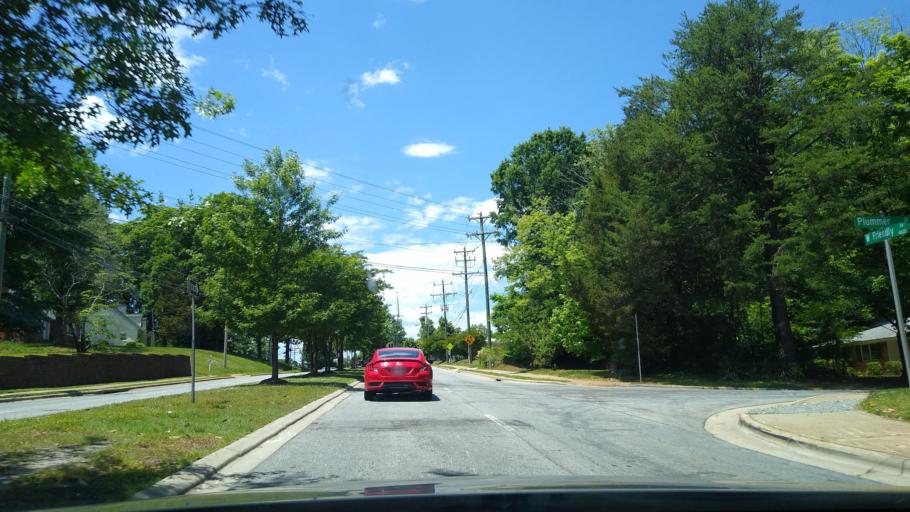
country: US
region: North Carolina
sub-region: Guilford County
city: Greensboro
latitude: 36.0918
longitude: -79.8670
